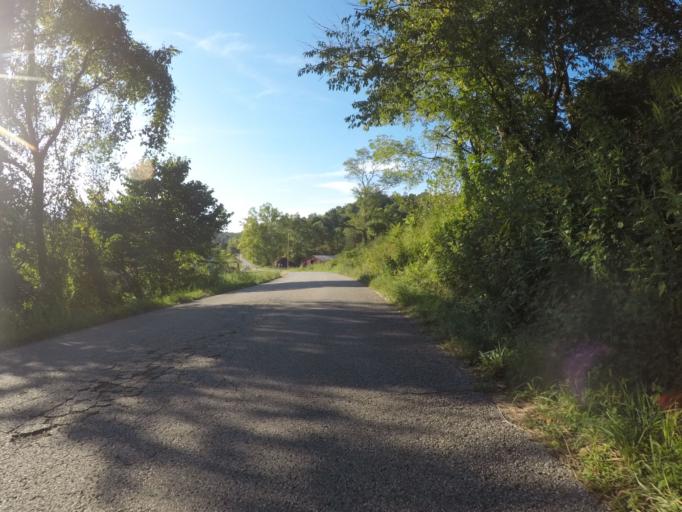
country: US
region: West Virginia
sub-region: Cabell County
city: Huntington
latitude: 38.5111
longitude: -82.4953
